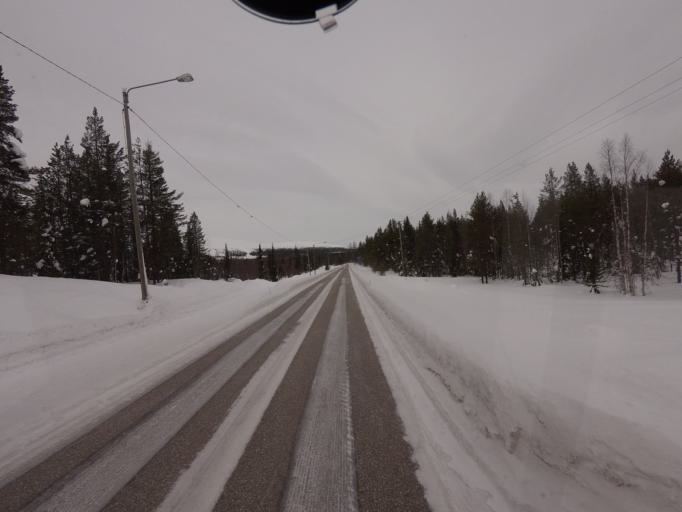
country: FI
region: Lapland
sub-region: Tunturi-Lappi
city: Kolari
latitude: 67.5345
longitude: 24.2779
